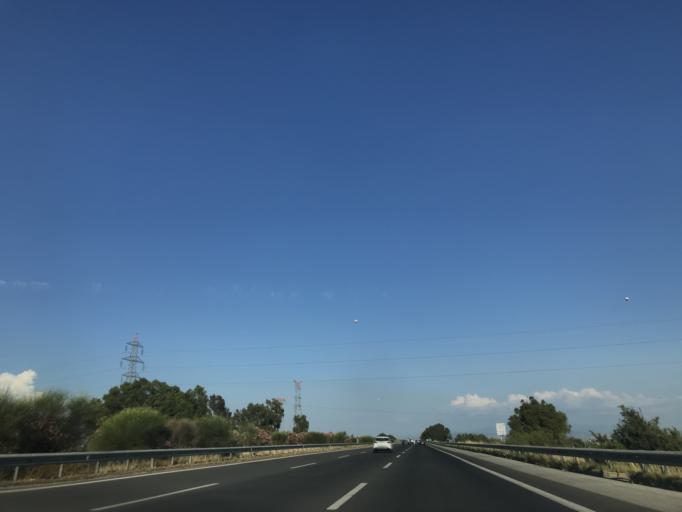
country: TR
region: Aydin
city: Germencik
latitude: 37.8737
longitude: 27.6221
